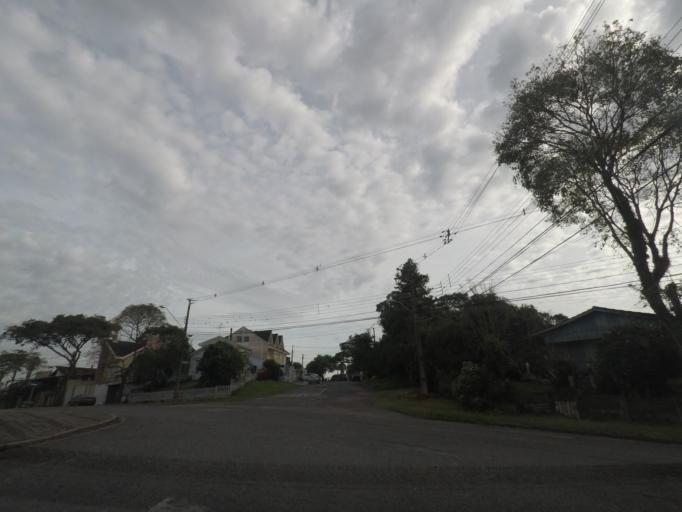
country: BR
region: Parana
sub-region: Curitiba
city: Curitiba
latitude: -25.4192
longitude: -49.2983
